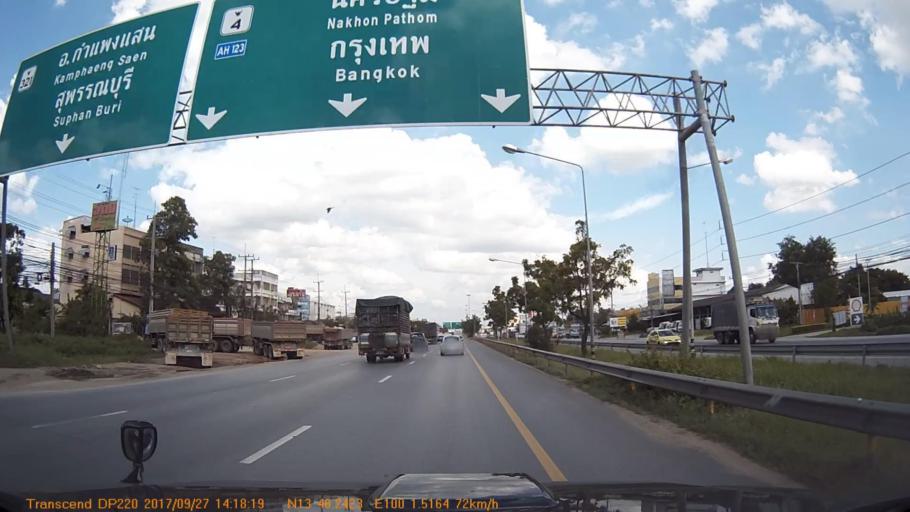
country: TH
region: Nakhon Pathom
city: Nakhon Pathom
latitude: 13.8040
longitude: 100.0252
